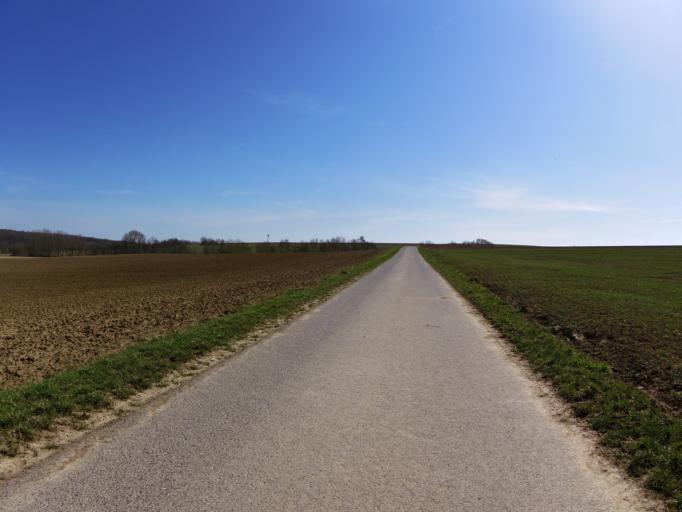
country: DE
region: Bavaria
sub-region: Regierungsbezirk Unterfranken
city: Prosselsheim
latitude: 49.8588
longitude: 10.1290
